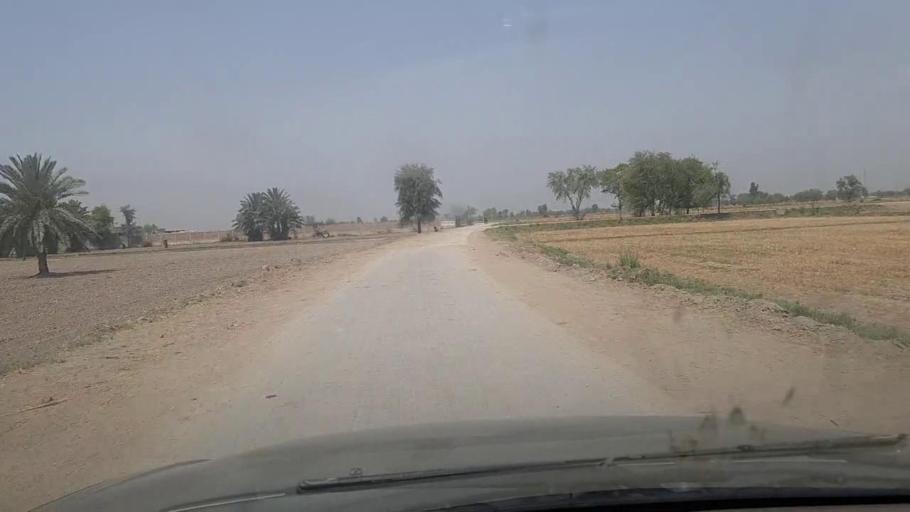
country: PK
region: Sindh
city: Adilpur
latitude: 27.9394
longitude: 69.3127
